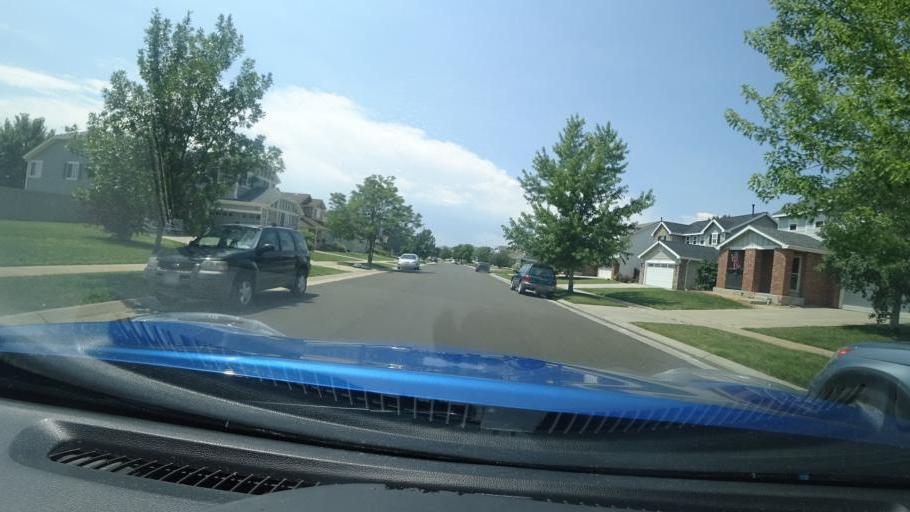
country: US
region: Colorado
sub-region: Adams County
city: Aurora
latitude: 39.6719
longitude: -104.7645
